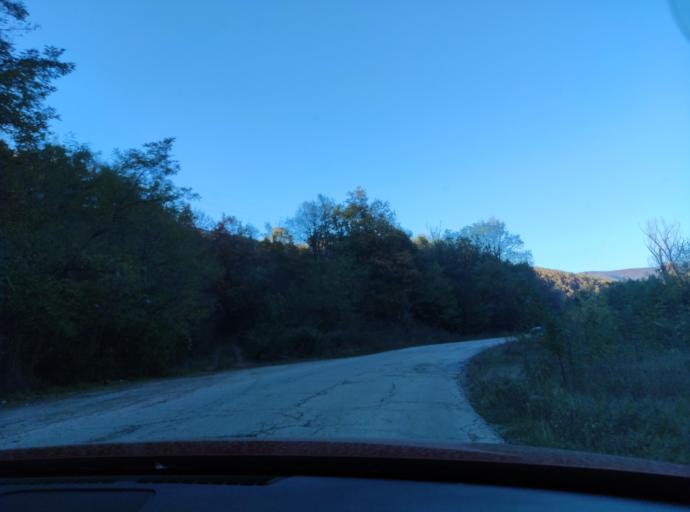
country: BG
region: Montana
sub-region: Obshtina Chiprovtsi
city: Chiprovtsi
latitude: 43.4060
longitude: 22.9378
